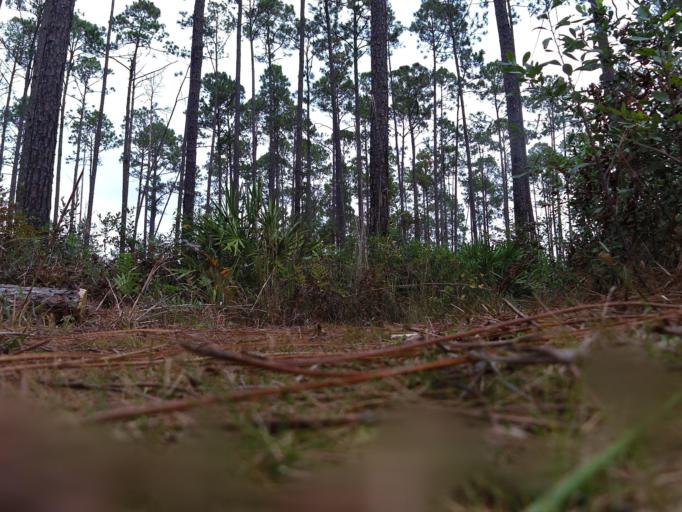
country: US
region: Georgia
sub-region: Charlton County
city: Folkston
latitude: 30.7131
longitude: -82.1617
